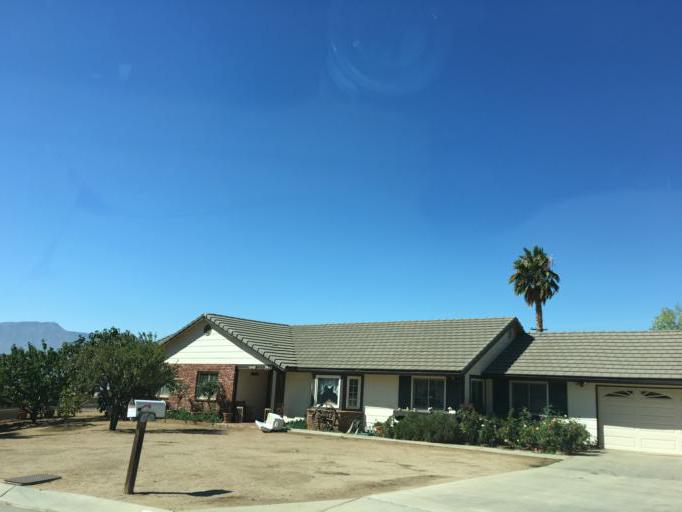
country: US
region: California
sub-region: Los Angeles County
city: Acton
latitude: 34.4997
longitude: -118.1978
